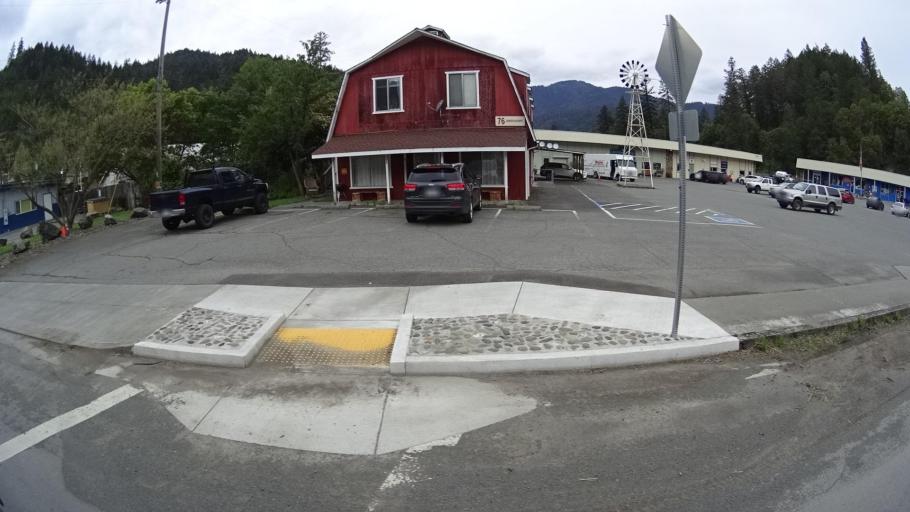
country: US
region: California
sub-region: Humboldt County
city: Willow Creek
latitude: 40.9403
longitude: -123.6292
